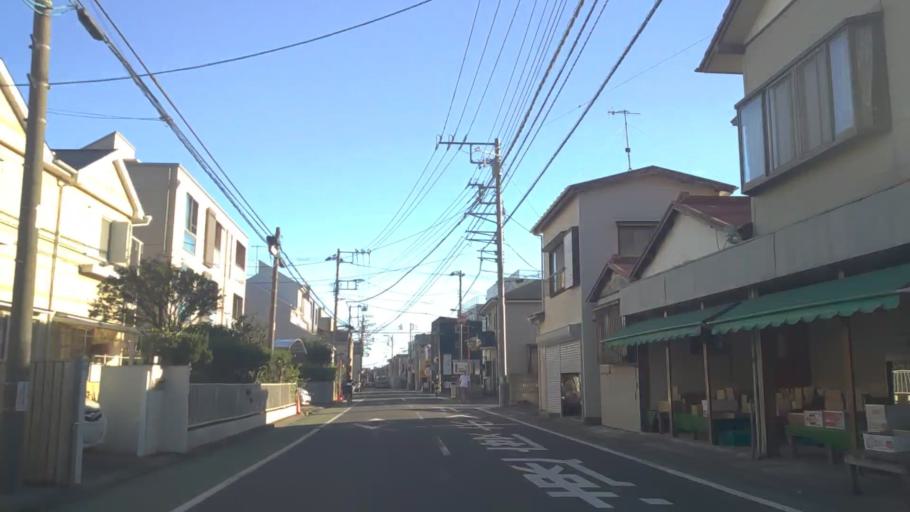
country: JP
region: Kanagawa
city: Chigasaki
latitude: 35.3295
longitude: 139.4145
